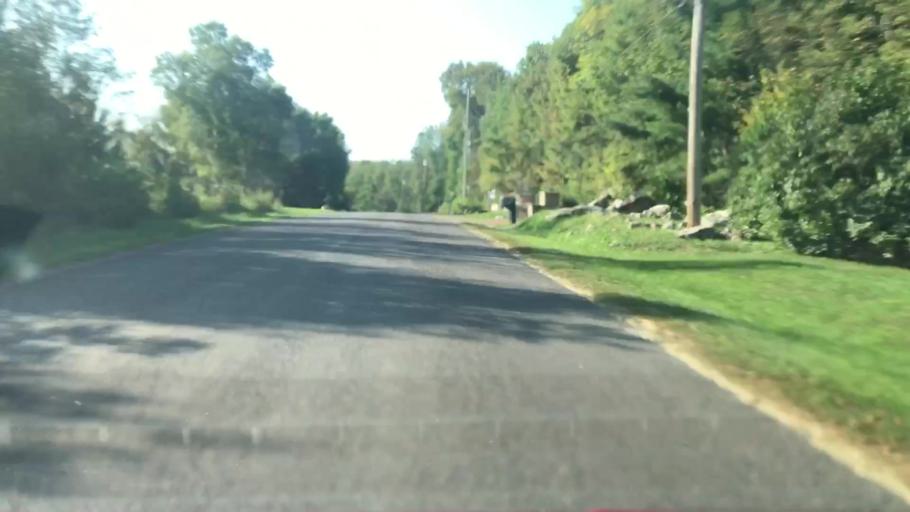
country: US
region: Michigan
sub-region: Chippewa County
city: Sault Ste. Marie
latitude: 46.2917
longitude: -84.0661
